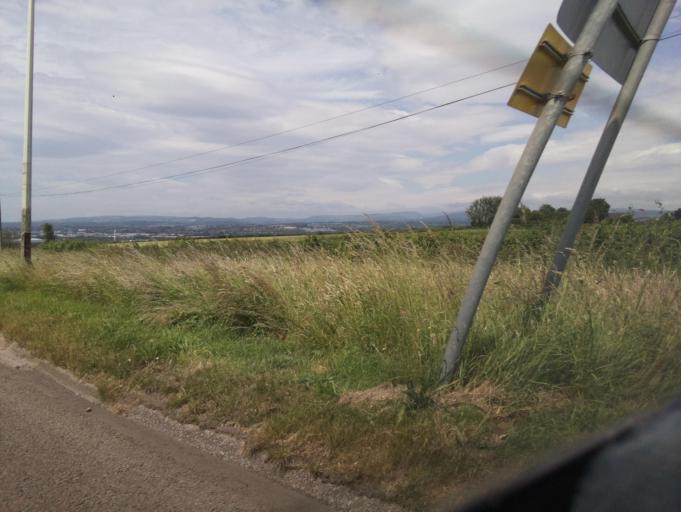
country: GB
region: Wales
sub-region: Vale of Glamorgan
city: Llangan
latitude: 51.4783
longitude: -3.5191
